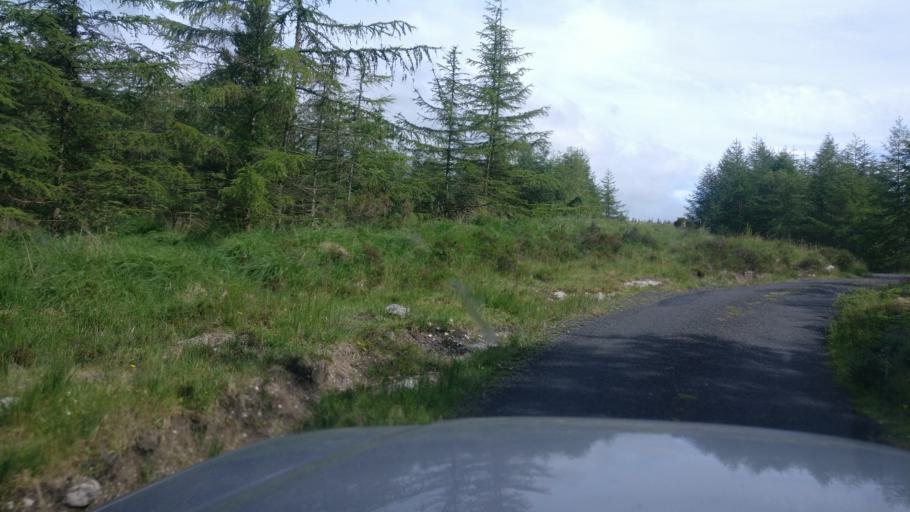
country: IE
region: Connaught
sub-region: County Galway
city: Gort
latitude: 53.0877
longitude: -8.6945
